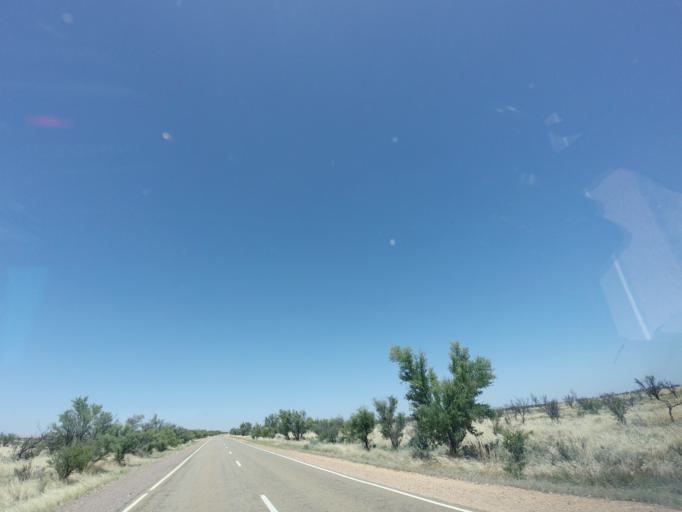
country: AU
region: South Australia
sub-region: Flinders Ranges
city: Quorn
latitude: -32.6670
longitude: 138.2267
